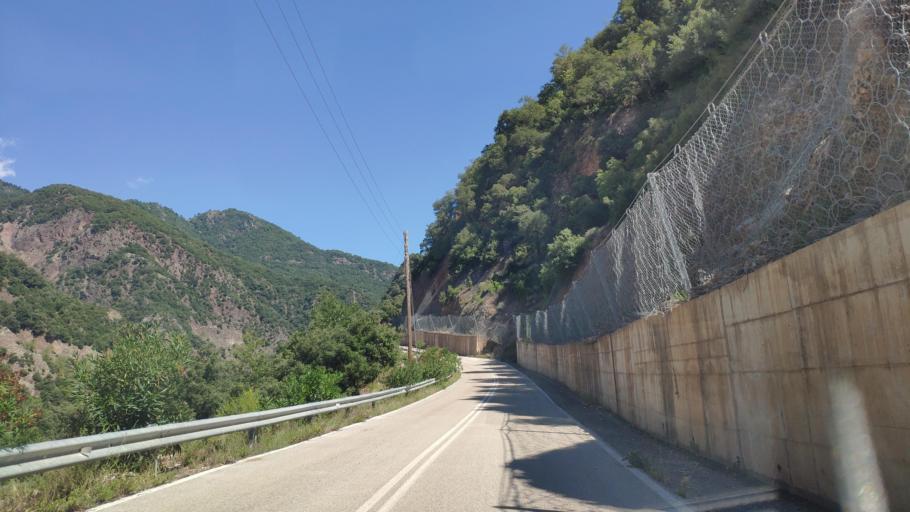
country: GR
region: Central Greece
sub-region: Nomos Evrytanias
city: Kerasochori
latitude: 39.0396
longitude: 21.5959
